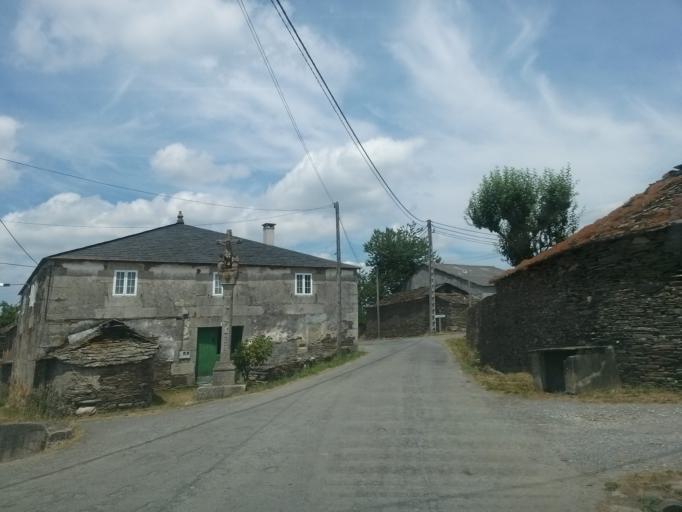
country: ES
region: Galicia
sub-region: Provincia de Lugo
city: Lugo
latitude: 43.0398
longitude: -7.6091
